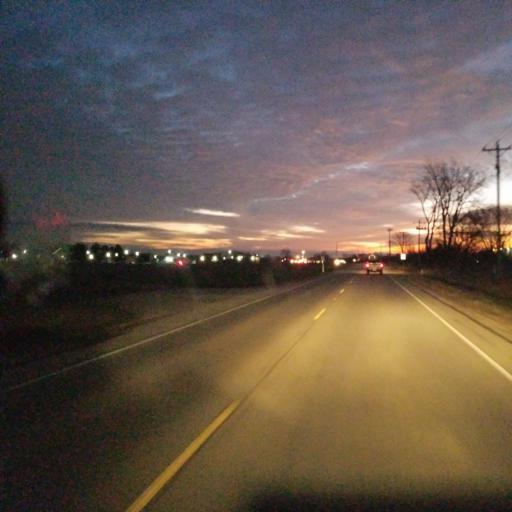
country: US
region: Illinois
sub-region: Peoria County
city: Bellevue
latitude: 40.6894
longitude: -89.7023
